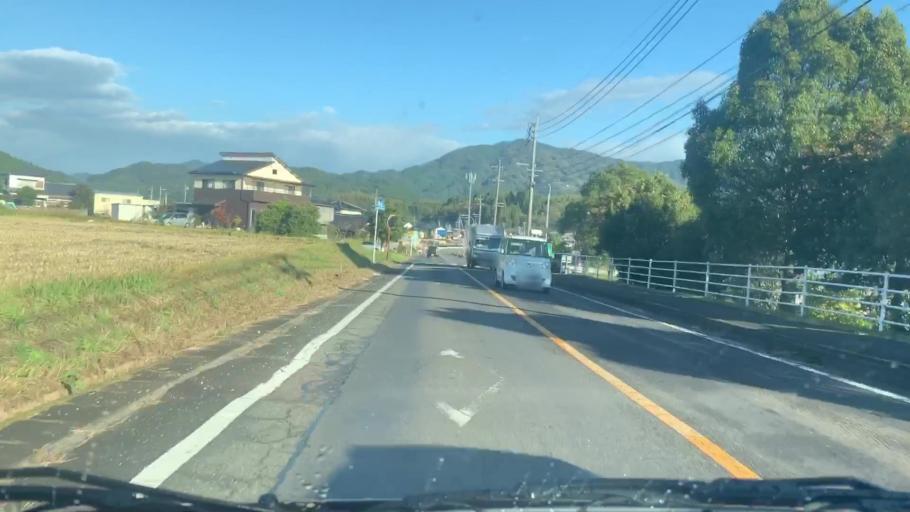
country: JP
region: Saga Prefecture
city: Takeocho-takeo
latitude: 33.2180
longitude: 130.0283
